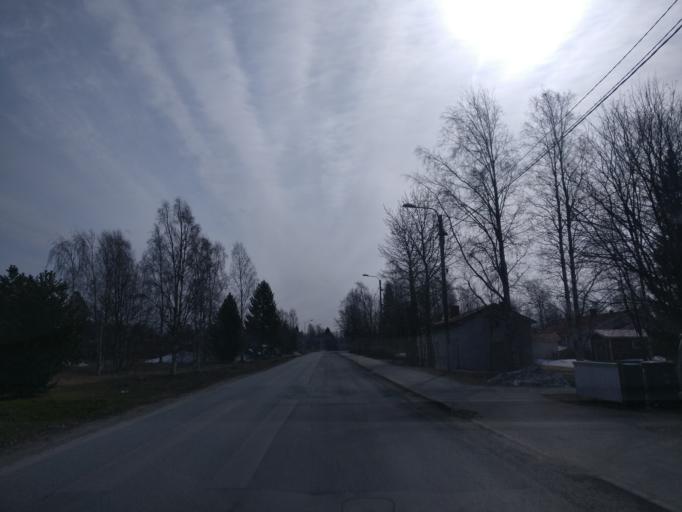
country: FI
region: Lapland
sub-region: Kemi-Tornio
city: Kemi
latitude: 65.7511
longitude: 24.5571
